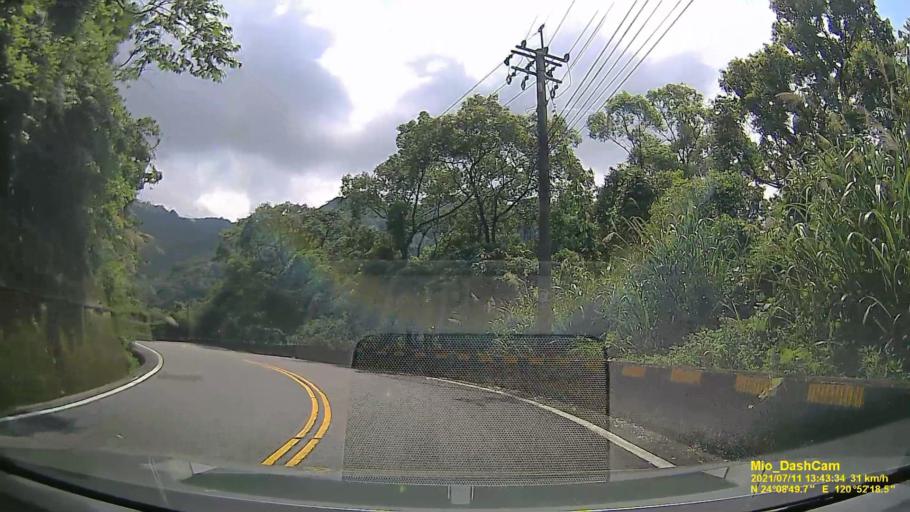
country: TW
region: Taiwan
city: Fengyuan
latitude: 24.1471
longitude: 120.8718
